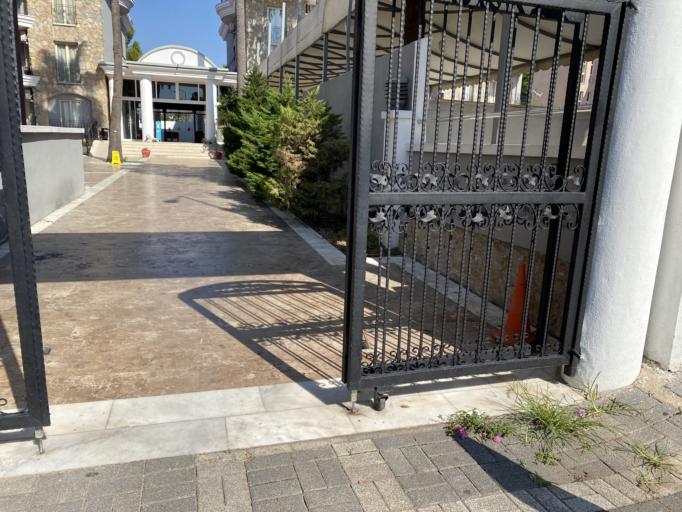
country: TR
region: Mugla
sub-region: Marmaris
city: Marmaris
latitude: 36.8452
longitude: 28.2517
